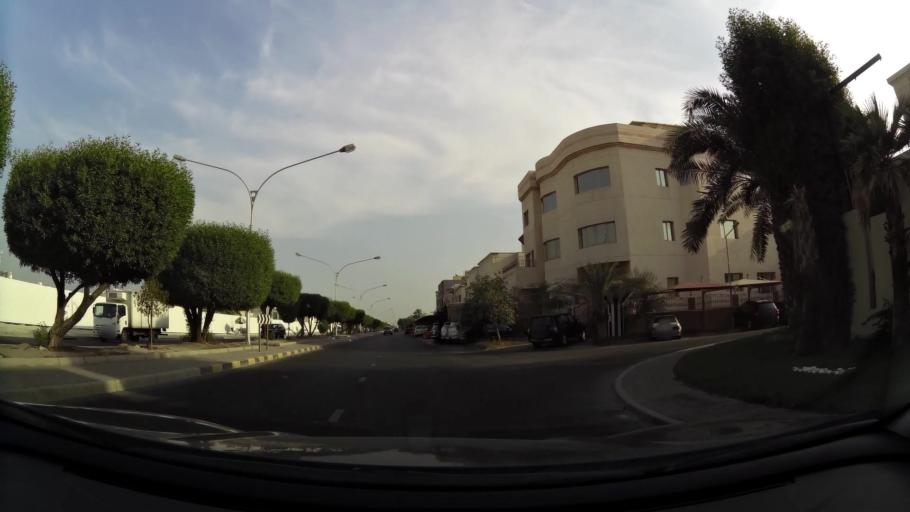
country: KW
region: Muhafazat Hawalli
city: Hawalli
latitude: 29.3196
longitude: 48.0059
